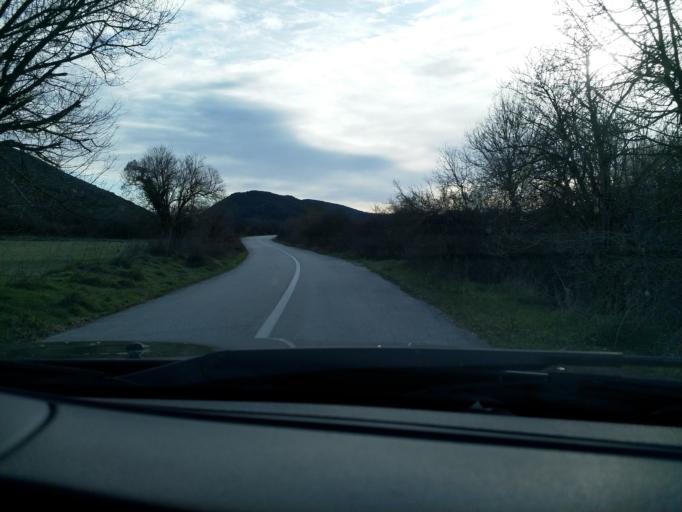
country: GR
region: Epirus
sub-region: Nomos Ioanninon
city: Asprangeloi
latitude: 39.8696
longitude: 20.7044
